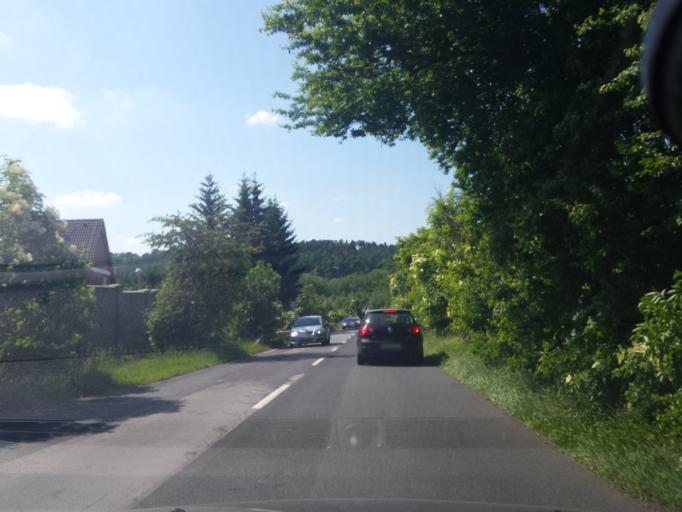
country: CZ
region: Central Bohemia
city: Kralupy nad Vltavou
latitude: 50.2198
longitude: 14.3000
